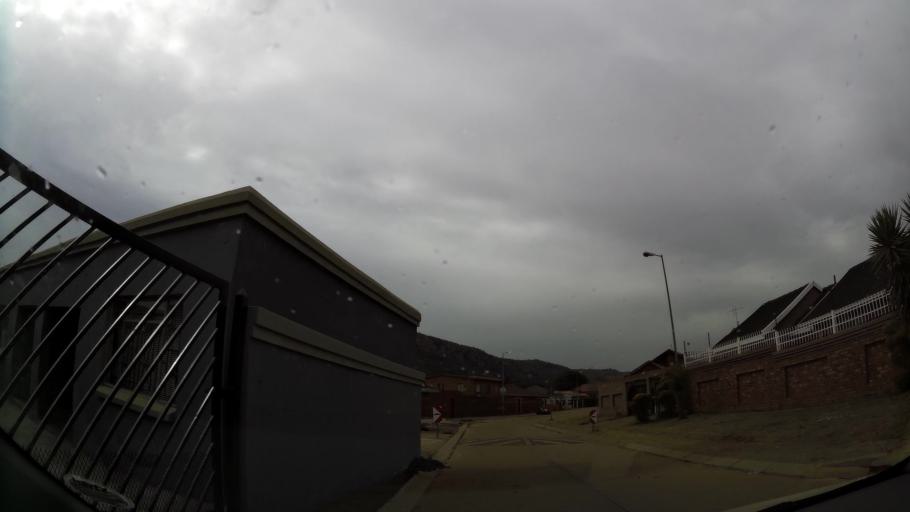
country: ZA
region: Gauteng
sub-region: City of Tshwane Metropolitan Municipality
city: Cullinan
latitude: -25.7045
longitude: 28.3577
